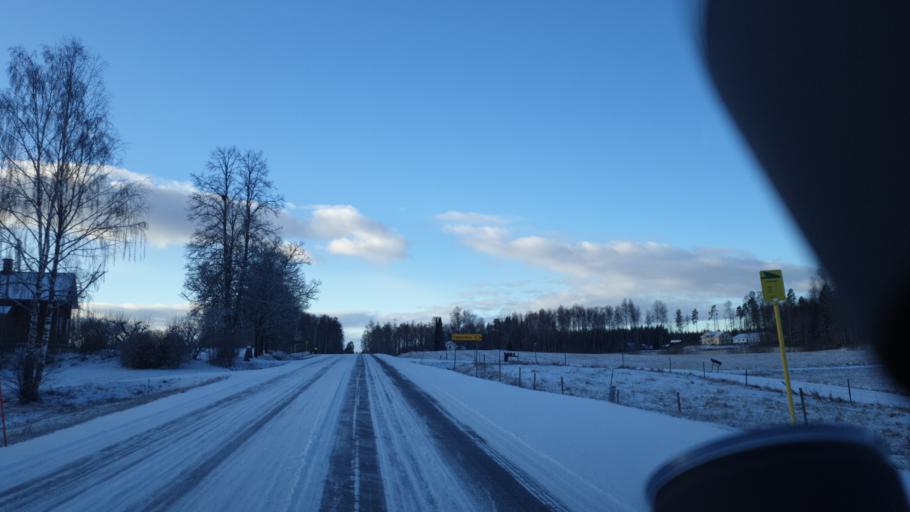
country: SE
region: Vaermland
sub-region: Arvika Kommun
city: Arvika
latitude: 59.6960
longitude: 12.6360
